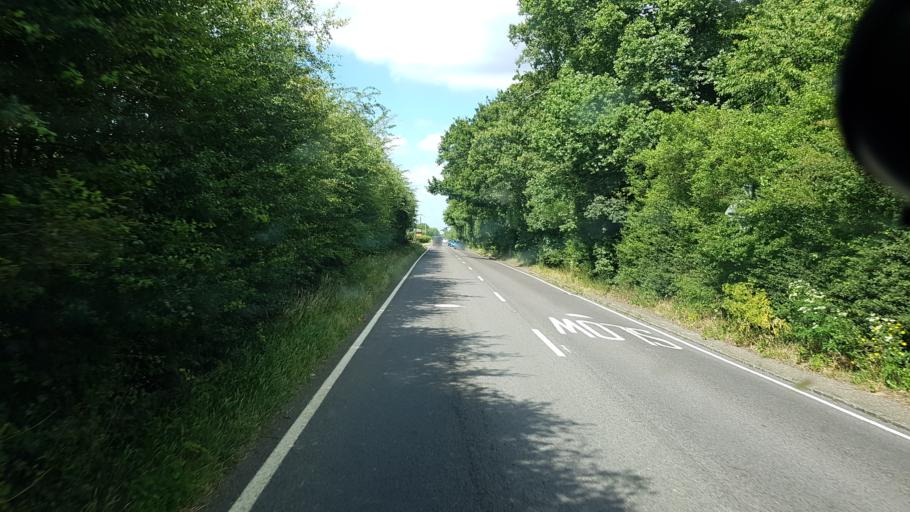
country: GB
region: England
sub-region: West Sussex
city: Billingshurst
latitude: 51.0367
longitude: -0.4413
